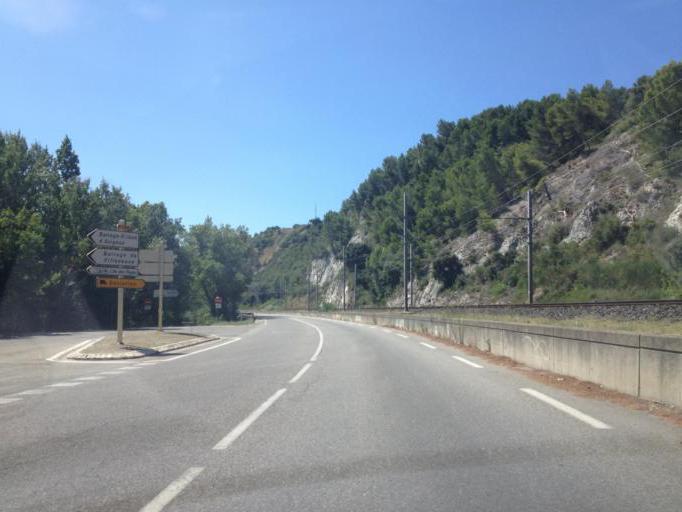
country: FR
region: Languedoc-Roussillon
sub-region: Departement du Gard
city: Villeneuve-les-Avignon
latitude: 43.9893
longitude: 4.8078
